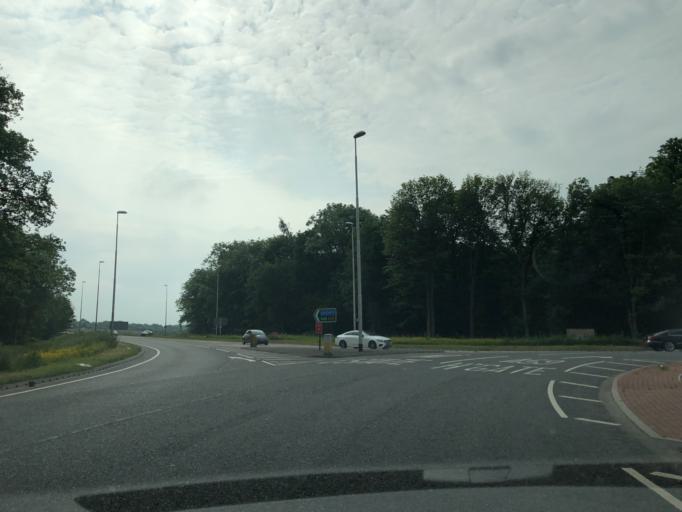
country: GB
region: England
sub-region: North Yorkshire
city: Boroughbridge
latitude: 54.0099
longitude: -1.3866
